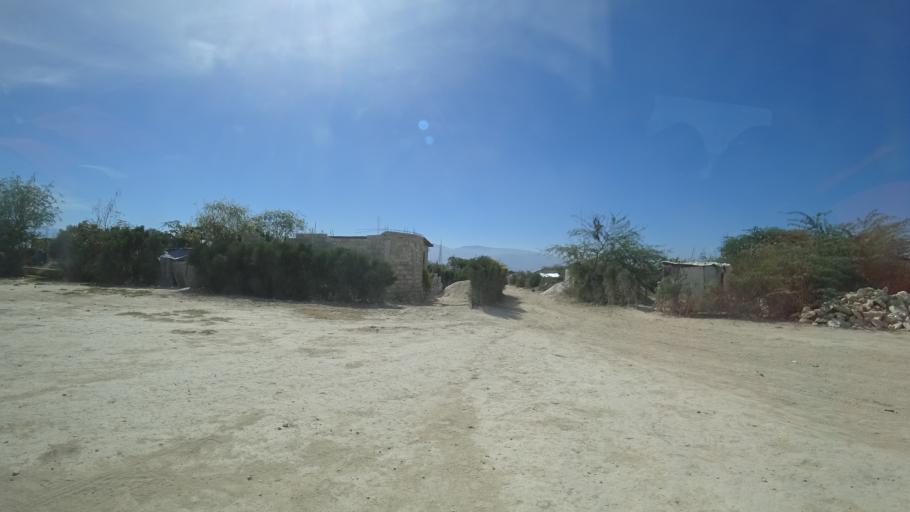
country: HT
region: Ouest
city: Croix des Bouquets
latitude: 18.6531
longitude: -72.2493
